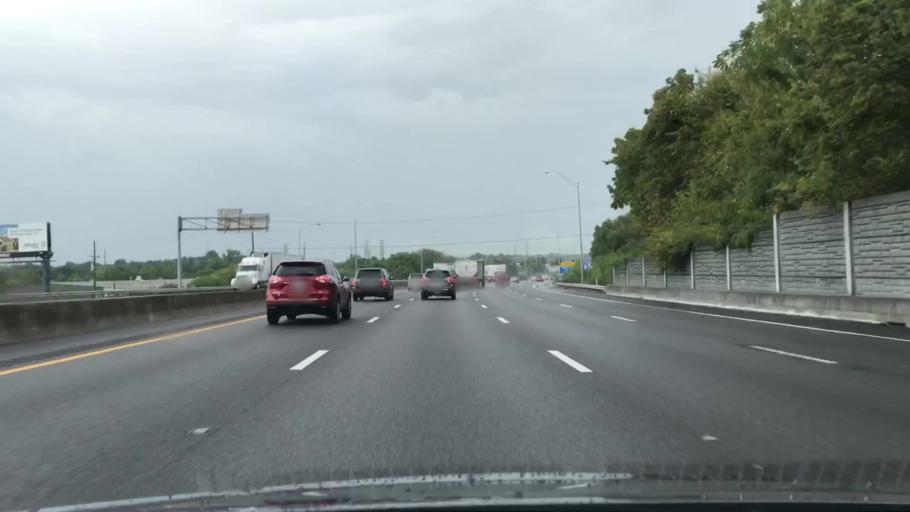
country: US
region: Tennessee
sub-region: Davidson County
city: Nashville
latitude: 36.1279
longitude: -86.7723
